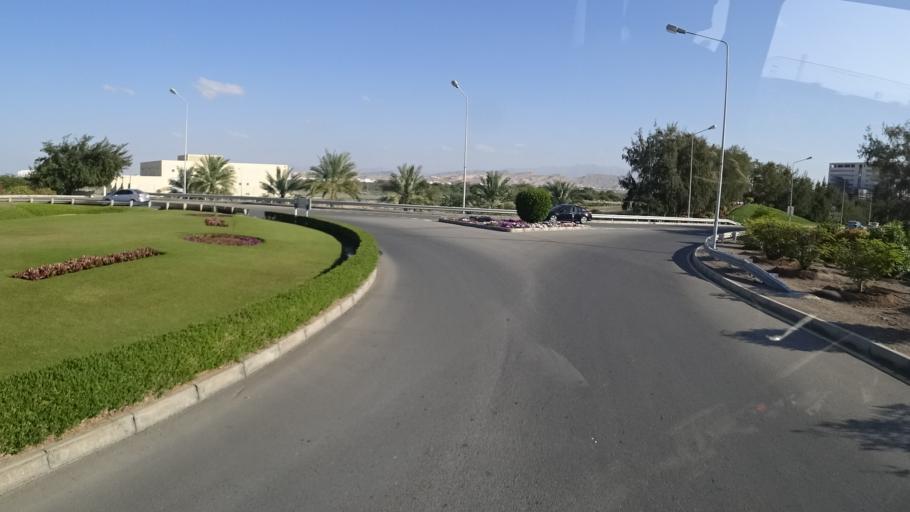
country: OM
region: Muhafazat Masqat
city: As Sib al Jadidah
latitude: 23.5871
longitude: 58.1769
